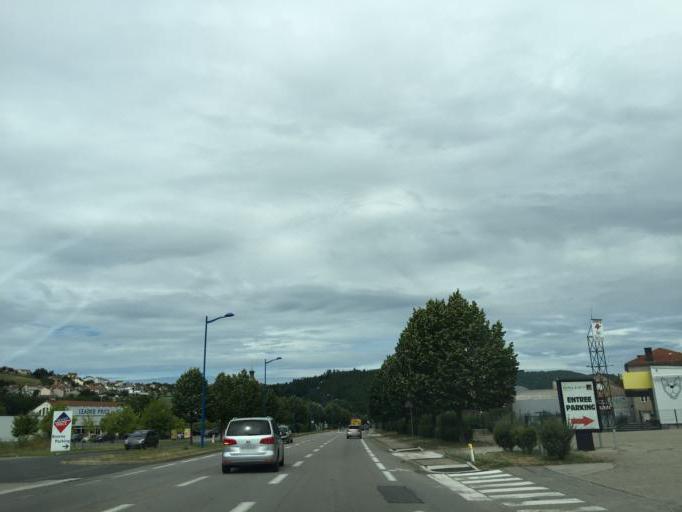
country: FR
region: Rhone-Alpes
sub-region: Departement de la Loire
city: Unieux
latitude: 45.3926
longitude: 4.2695
